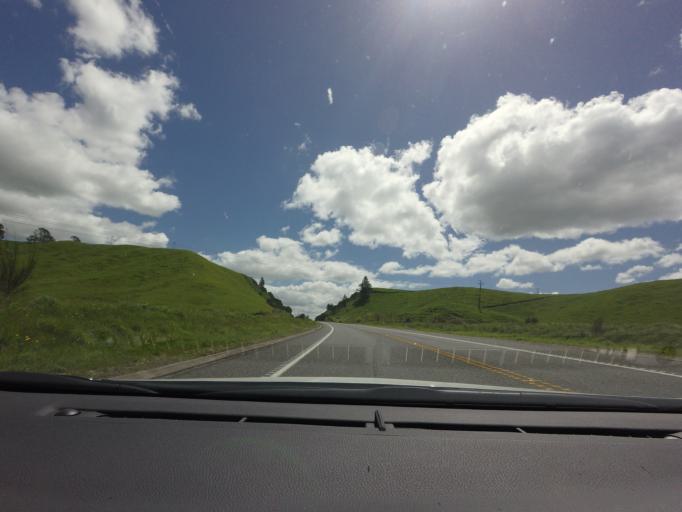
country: NZ
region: Bay of Plenty
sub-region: Rotorua District
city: Rotorua
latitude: -38.2668
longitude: 176.3296
